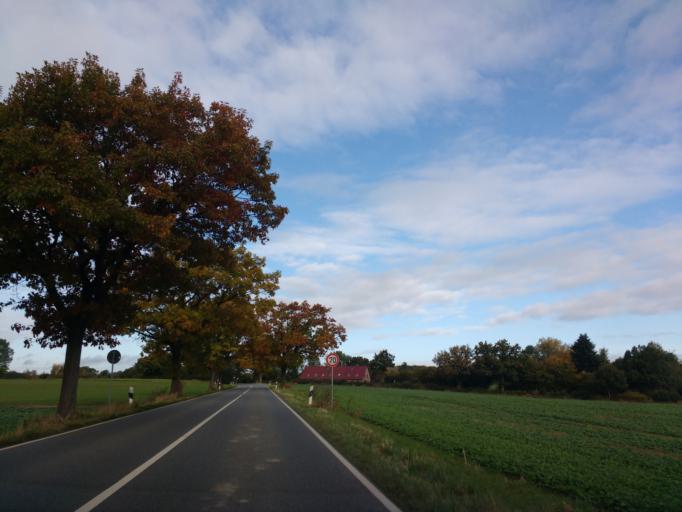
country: DE
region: Schleswig-Holstein
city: Altenkrempe
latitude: 54.1553
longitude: 10.8144
